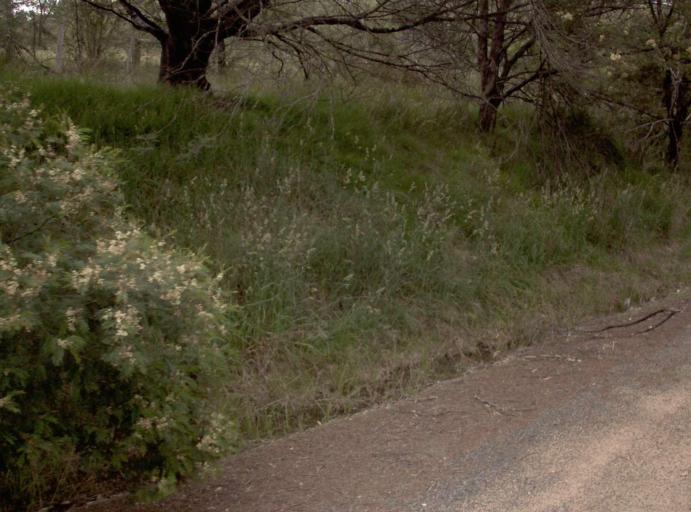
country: AU
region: New South Wales
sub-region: Bombala
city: Bombala
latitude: -37.3337
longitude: 149.2062
